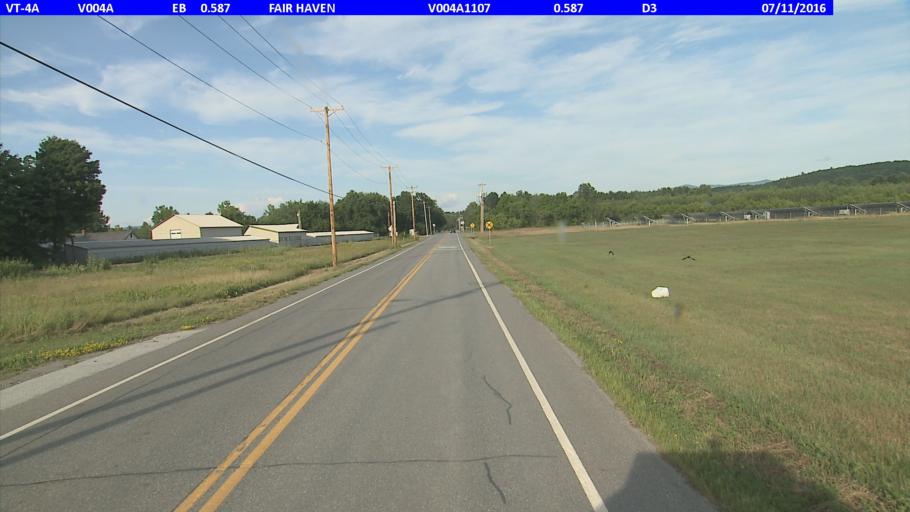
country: US
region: Vermont
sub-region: Rutland County
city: Fair Haven
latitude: 43.5861
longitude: -73.2818
